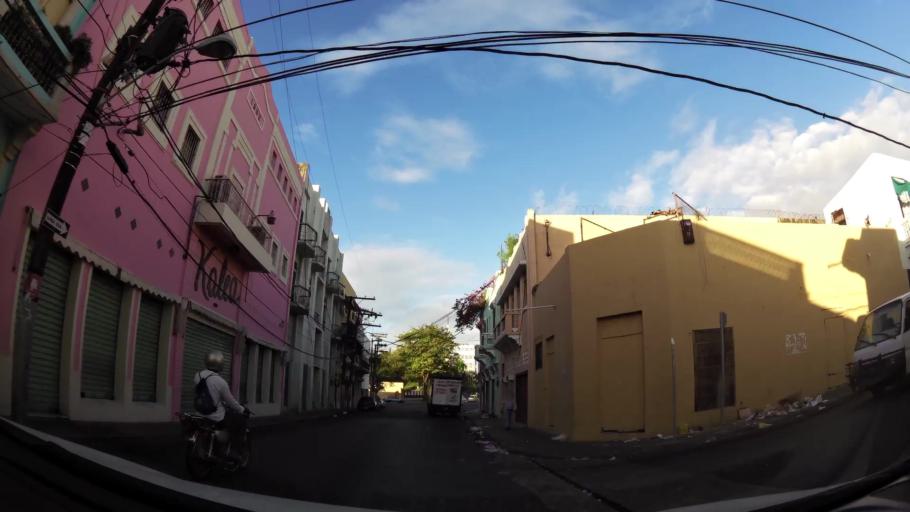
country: DO
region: Nacional
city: Ciudad Nueva
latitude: 18.4725
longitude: -69.8909
